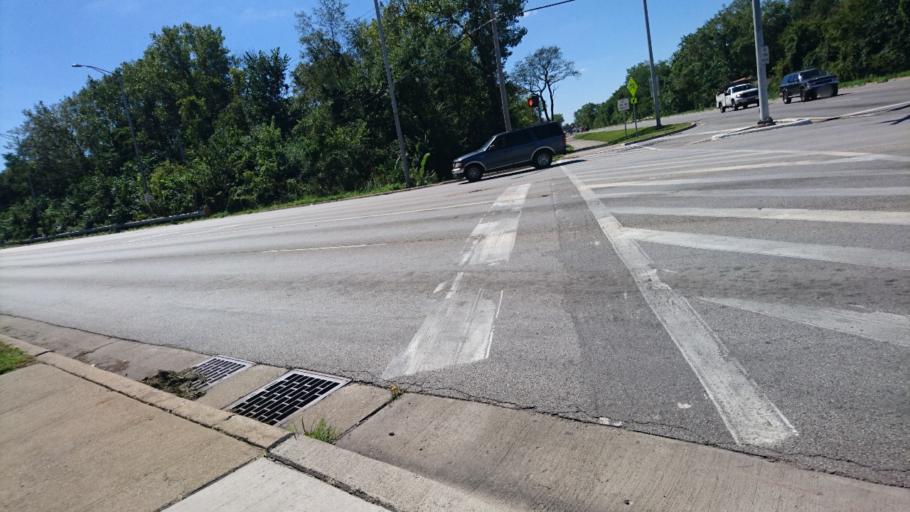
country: US
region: Illinois
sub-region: Cook County
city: Chicago Heights
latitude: 41.5150
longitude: -87.6355
